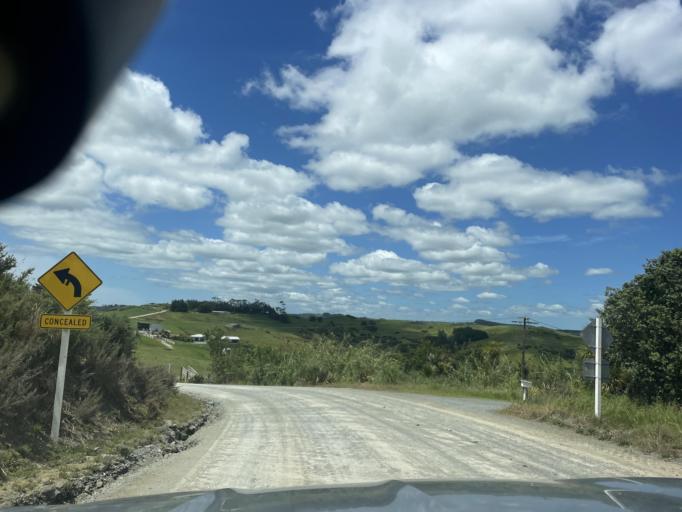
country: NZ
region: Auckland
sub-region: Auckland
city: Wellsford
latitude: -36.1369
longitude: 174.5356
